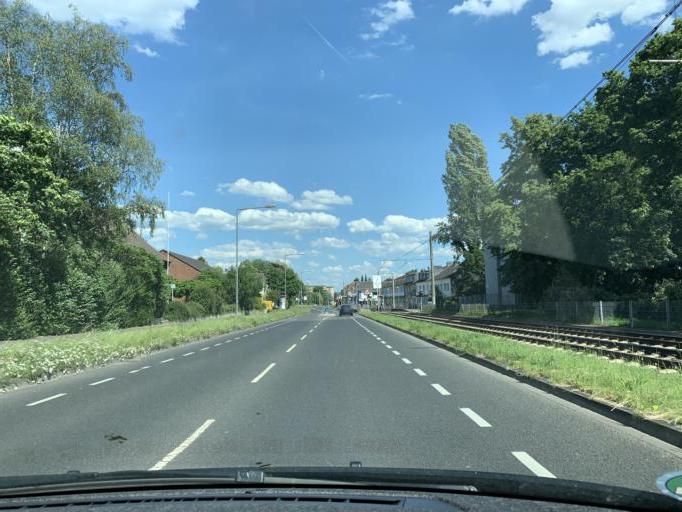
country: DE
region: North Rhine-Westphalia
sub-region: Regierungsbezirk Koln
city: Bilderstoeckchen
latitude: 50.9949
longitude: 6.9236
